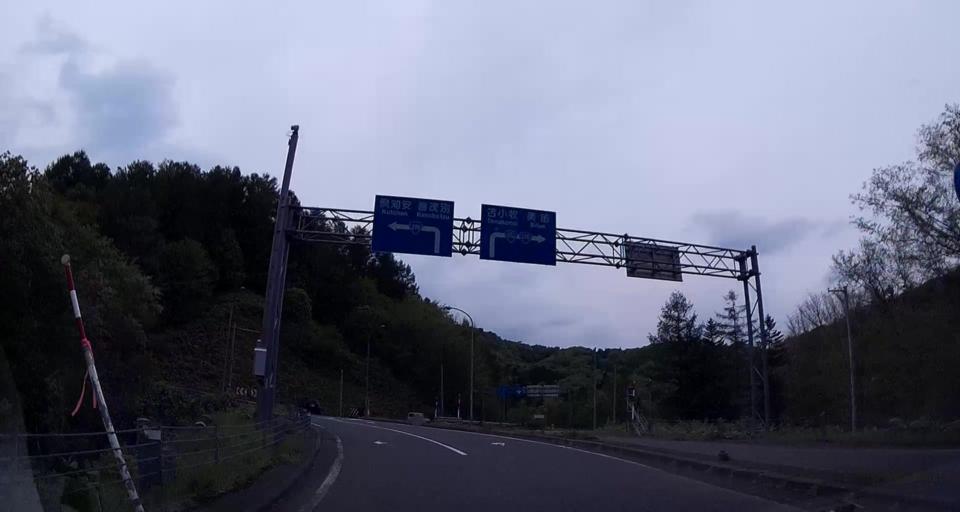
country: JP
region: Hokkaido
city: Shiraoi
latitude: 42.6951
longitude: 141.1065
